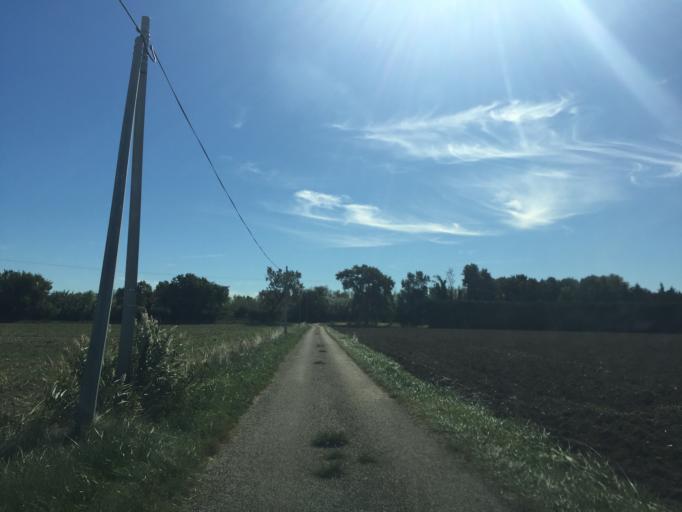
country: FR
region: Provence-Alpes-Cote d'Azur
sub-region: Departement du Vaucluse
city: Piolenc
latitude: 44.1519
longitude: 4.7700
